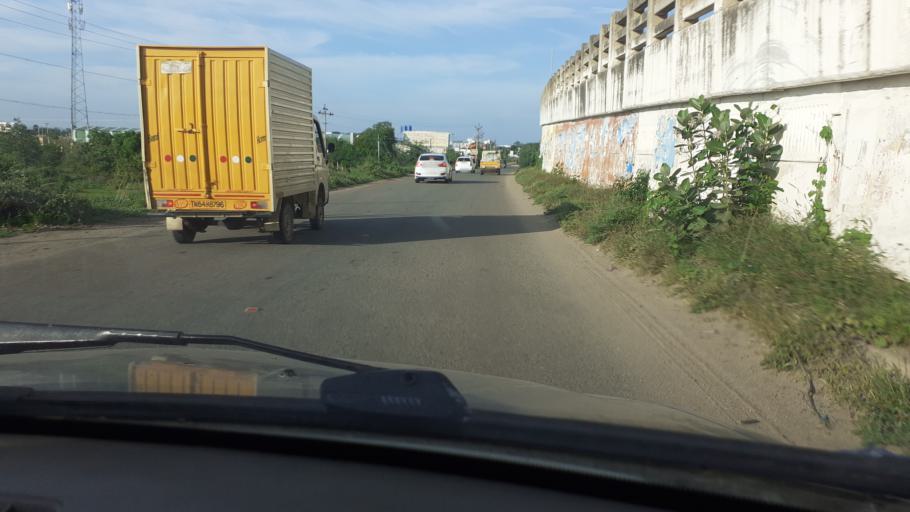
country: IN
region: Tamil Nadu
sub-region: Tirunelveli Kattabo
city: Tirunelveli
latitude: 8.6577
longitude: 77.7138
